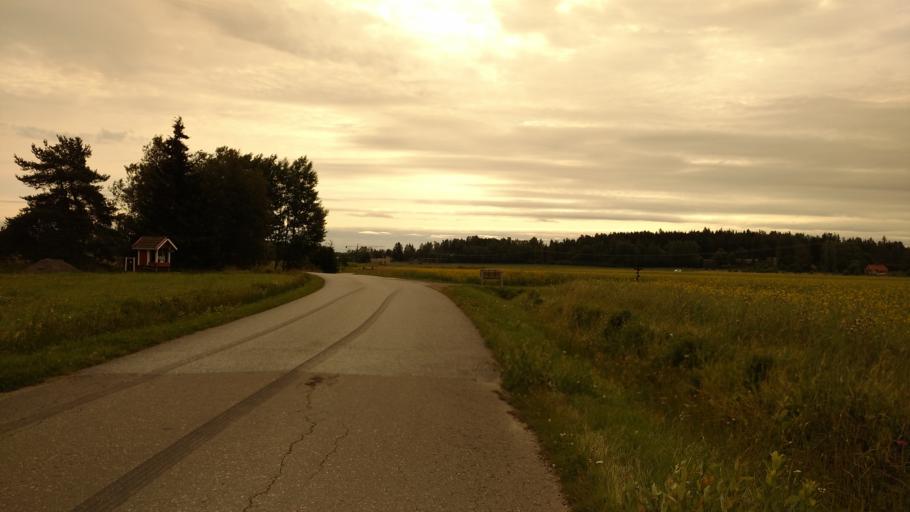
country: FI
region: Varsinais-Suomi
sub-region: Turku
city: Piikkioe
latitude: 60.4288
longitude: 22.4626
